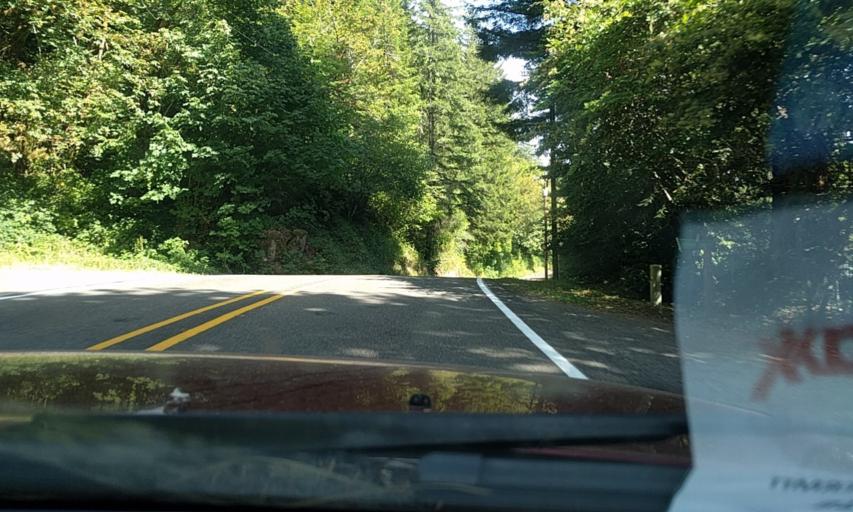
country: US
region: Oregon
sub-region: Lane County
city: Florence
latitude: 44.0414
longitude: -123.8654
